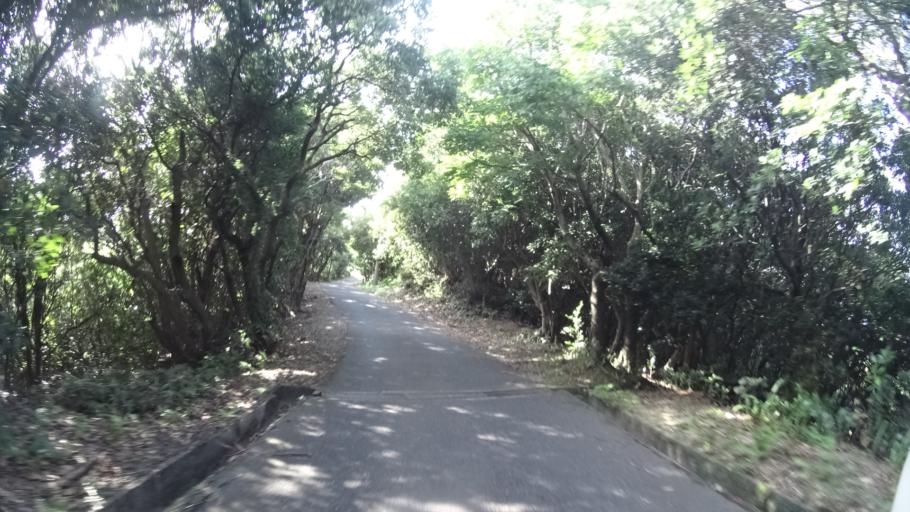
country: JP
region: Kagoshima
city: Nishinoomote
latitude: 30.3898
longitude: 130.3853
